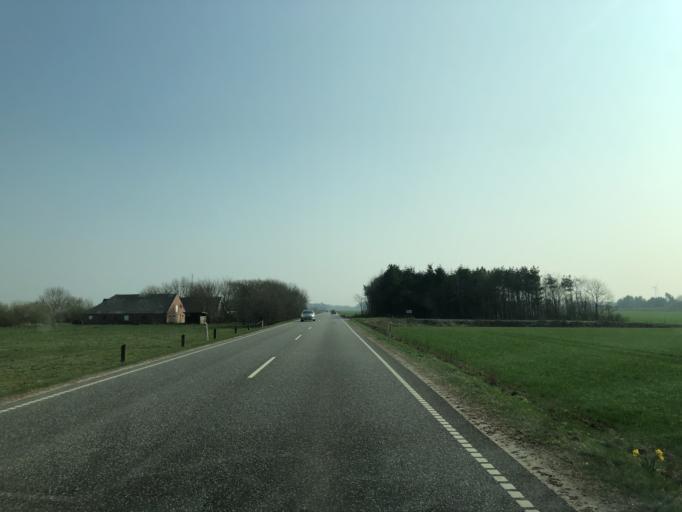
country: DK
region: Central Jutland
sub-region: Ringkobing-Skjern Kommune
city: Videbaek
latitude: 56.0979
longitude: 8.5076
